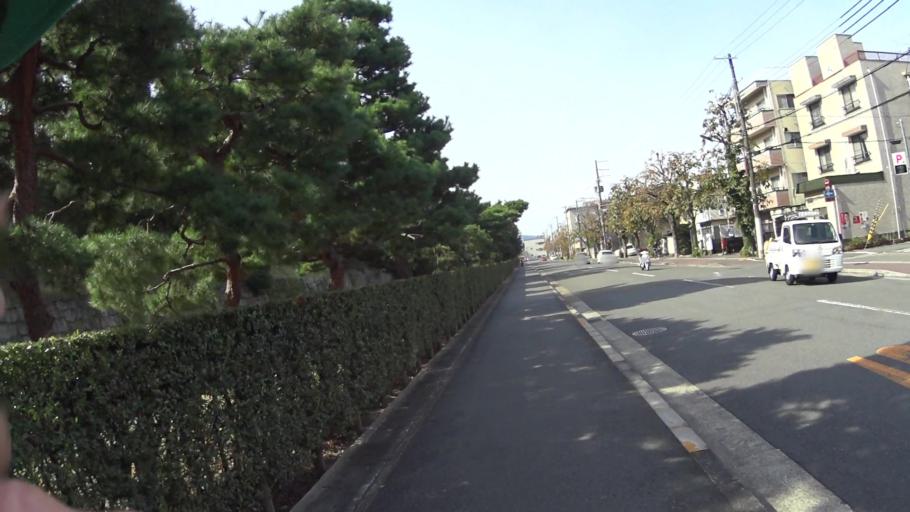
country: JP
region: Kyoto
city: Kyoto
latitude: 35.0158
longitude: 135.7486
